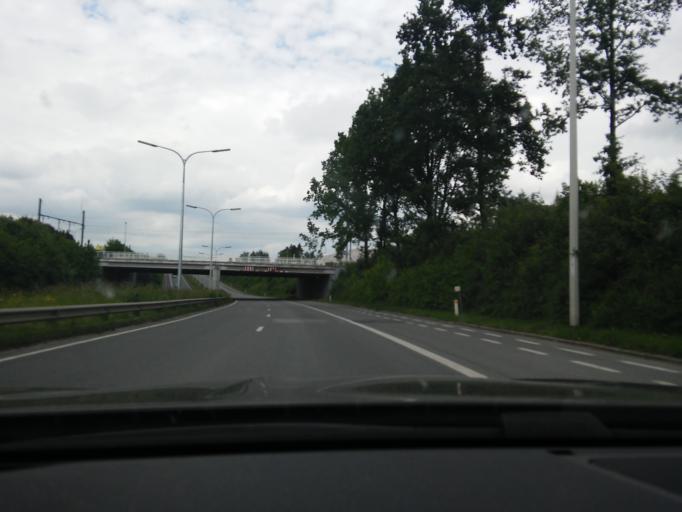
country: BE
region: Flanders
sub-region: Provincie Oost-Vlaanderen
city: Ninove
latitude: 50.8404
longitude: 4.0369
